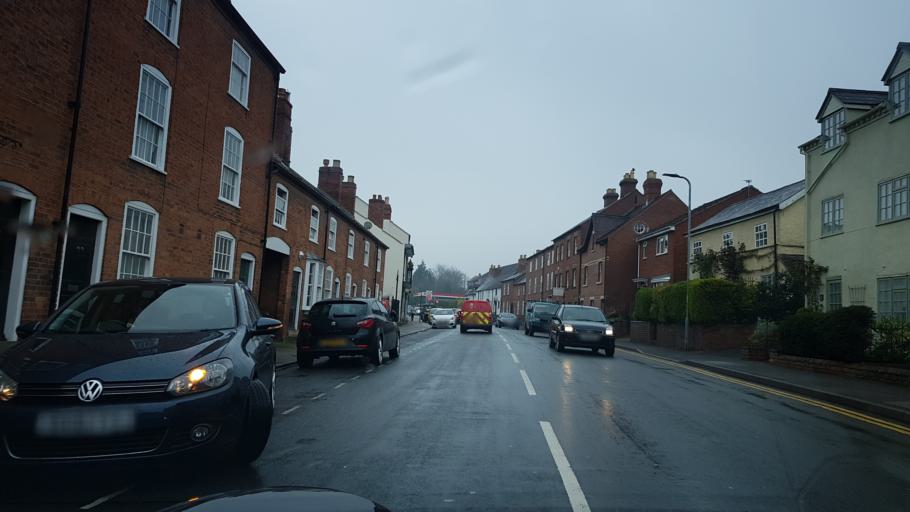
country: GB
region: England
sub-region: Herefordshire
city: Ledbury
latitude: 52.0400
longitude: -2.4247
